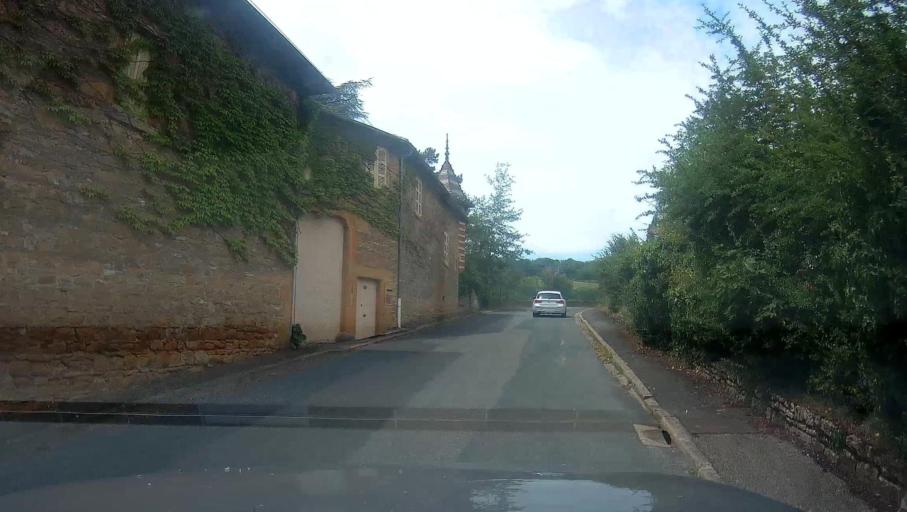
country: FR
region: Rhone-Alpes
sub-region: Departement du Rhone
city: Theize
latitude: 45.9276
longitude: 4.6185
